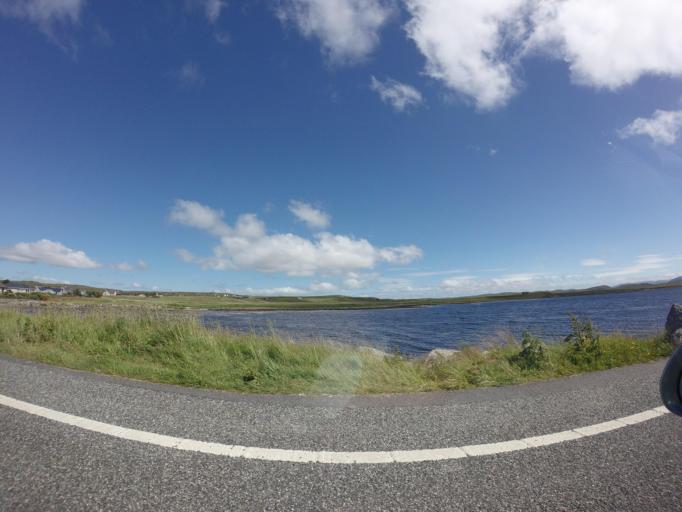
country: GB
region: Scotland
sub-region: Eilean Siar
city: Harris
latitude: 58.1966
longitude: -6.7415
